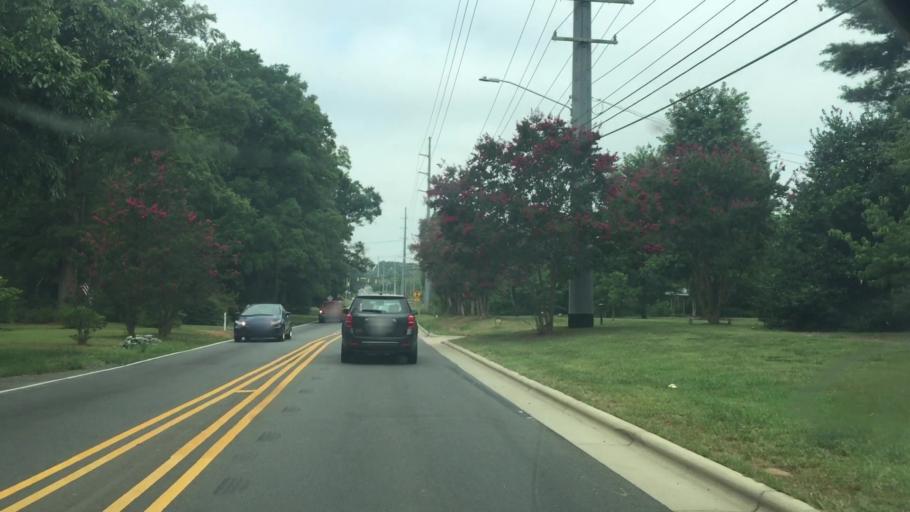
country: US
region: North Carolina
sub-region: Cabarrus County
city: Concord
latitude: 35.4145
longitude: -80.6507
